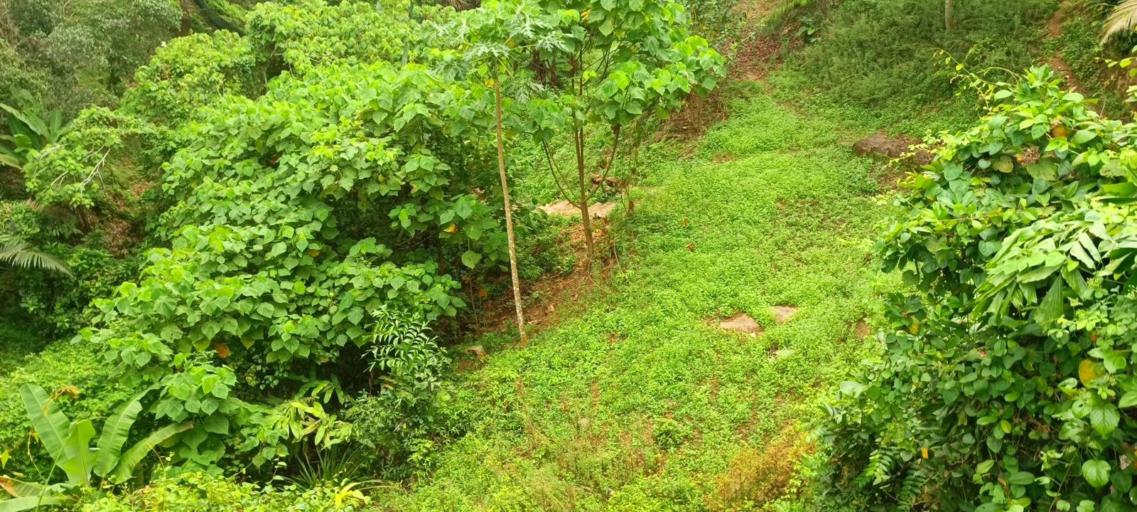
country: MY
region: Penang
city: Bukit Mertajam
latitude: 5.3740
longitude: 100.4959
